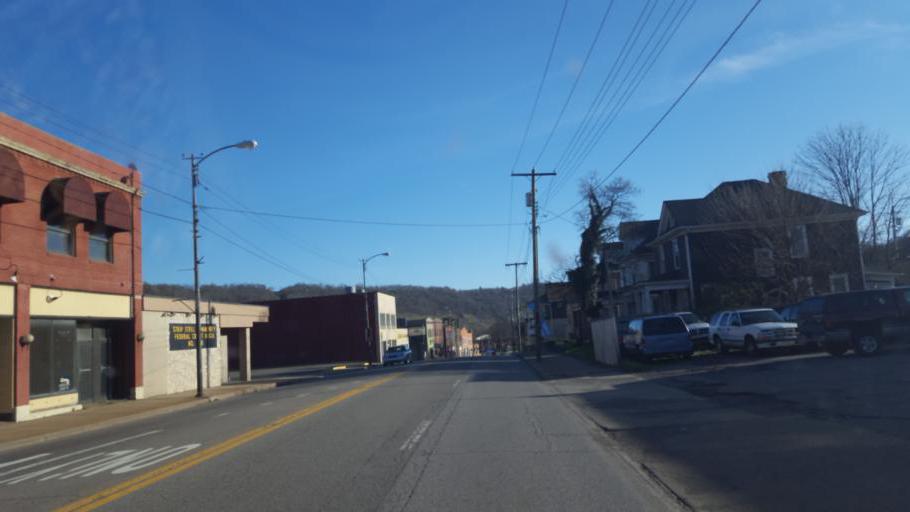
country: US
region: West Virginia
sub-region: Hancock County
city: Weirton
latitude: 40.4040
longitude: -80.5888
